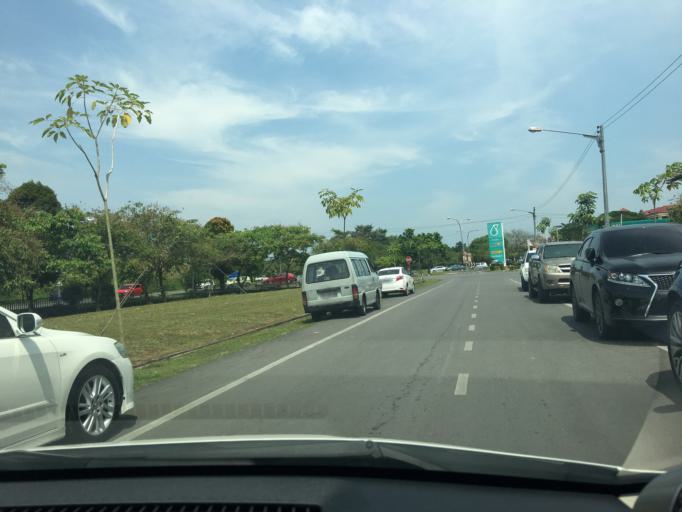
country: MY
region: Sarawak
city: Kuching
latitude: 1.5139
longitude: 110.3132
